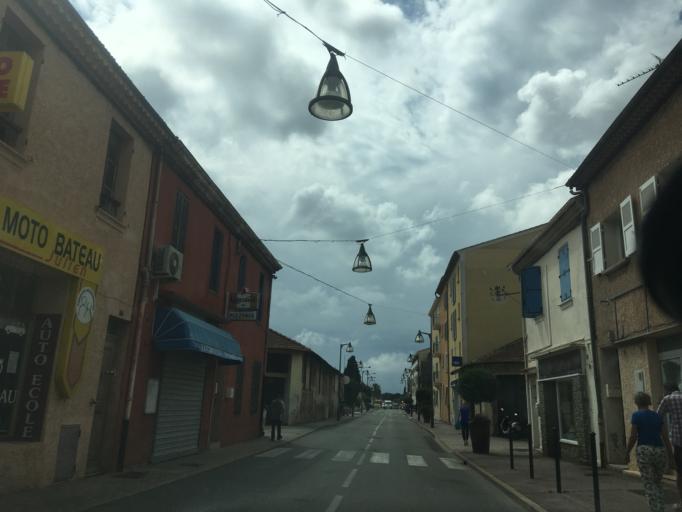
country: FR
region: Provence-Alpes-Cote d'Azur
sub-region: Departement du Var
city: La Londe-les-Maures
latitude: 43.1374
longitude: 6.2349
